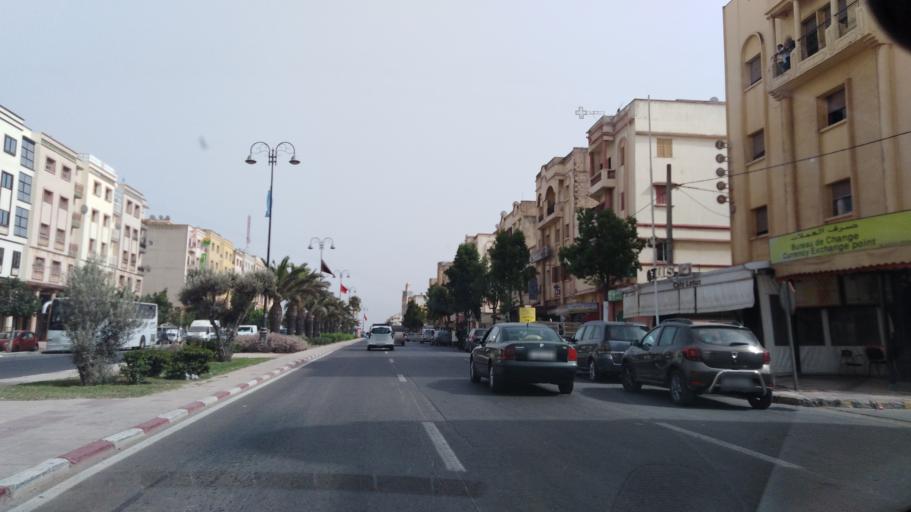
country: MA
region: Chaouia-Ouardigha
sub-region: Settat Province
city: Berrechid
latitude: 33.2739
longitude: -7.5872
